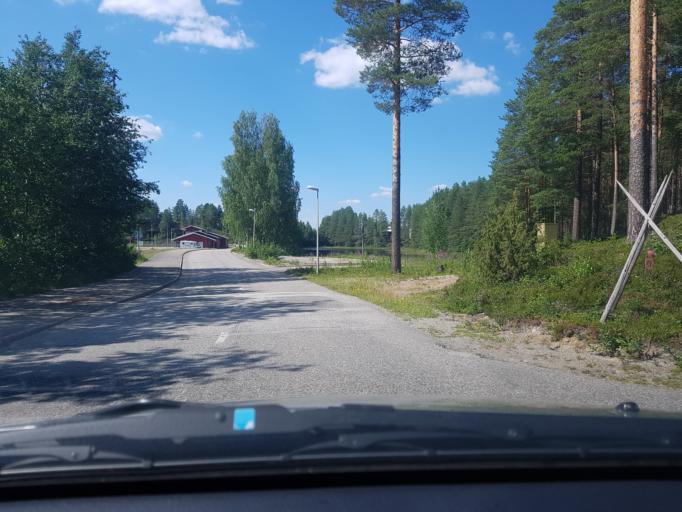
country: FI
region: Kainuu
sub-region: Kehys-Kainuu
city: Kuhmo
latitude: 64.1186
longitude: 29.5864
